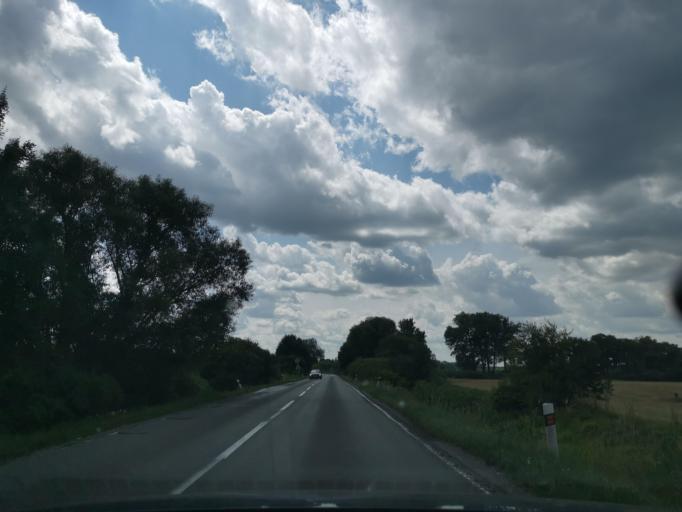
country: CZ
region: South Moravian
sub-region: Okres Breclav
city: Lanzhot
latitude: 48.6442
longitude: 17.0076
